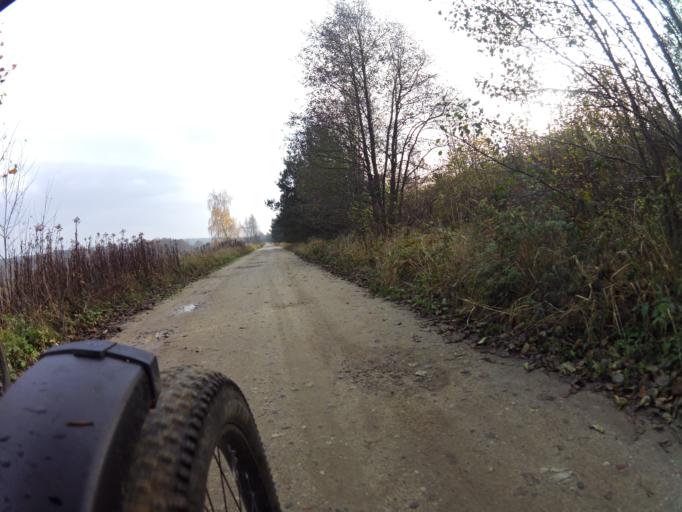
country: PL
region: Pomeranian Voivodeship
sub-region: Powiat wejherowski
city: Orle
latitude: 54.7019
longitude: 18.1088
